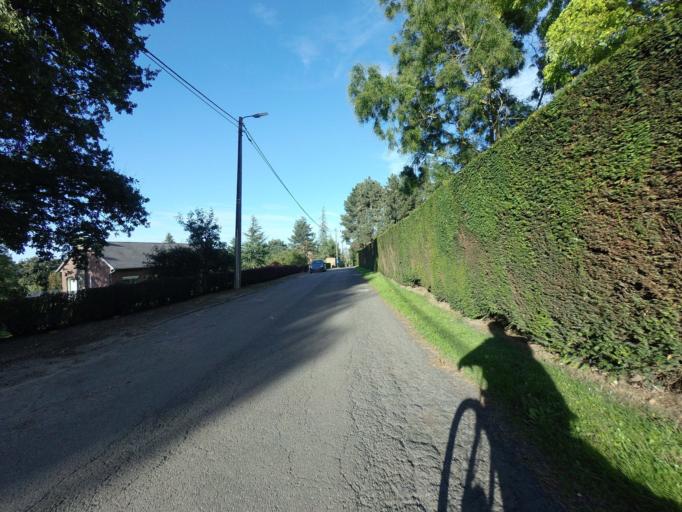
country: BE
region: Flanders
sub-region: Provincie Vlaams-Brabant
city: Leuven
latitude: 50.8995
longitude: 4.6934
